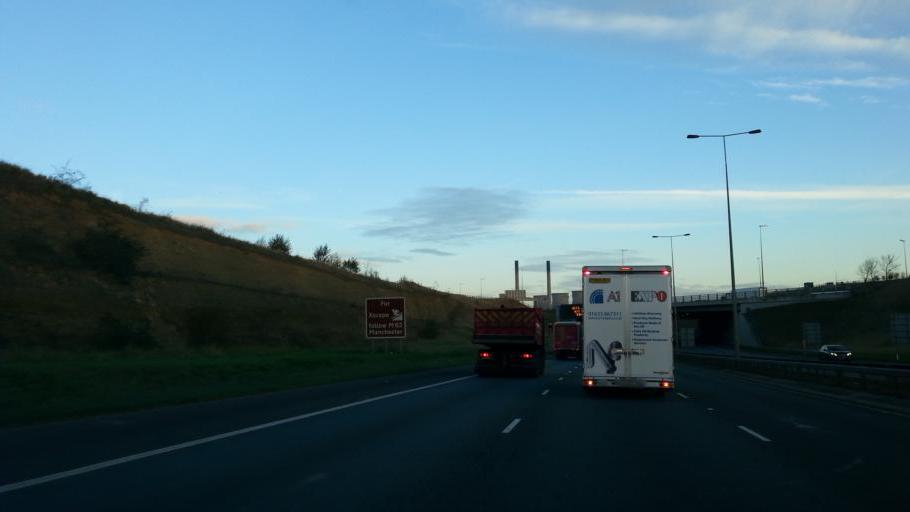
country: GB
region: England
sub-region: City and Borough of Wakefield
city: Ferrybridge
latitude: 53.6967
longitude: -1.2756
